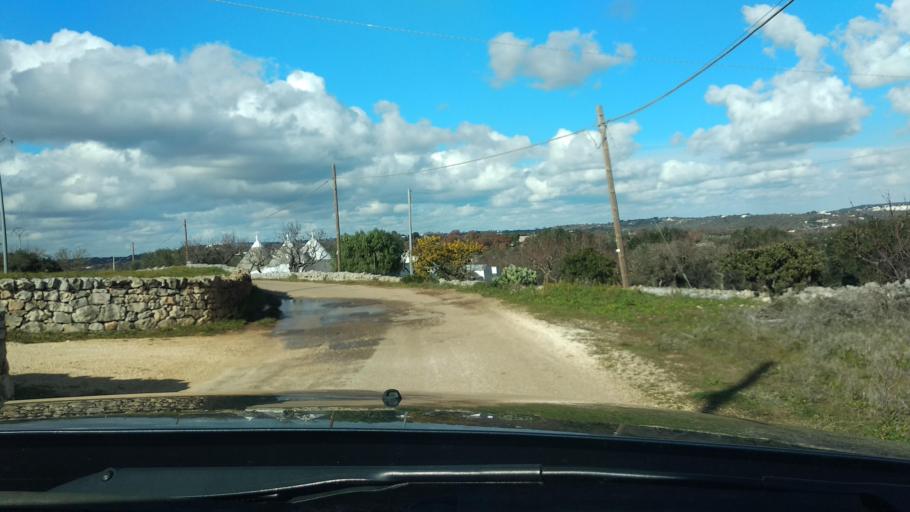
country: IT
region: Apulia
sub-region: Provincia di Brindisi
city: Casalini
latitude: 40.7035
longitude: 17.4573
